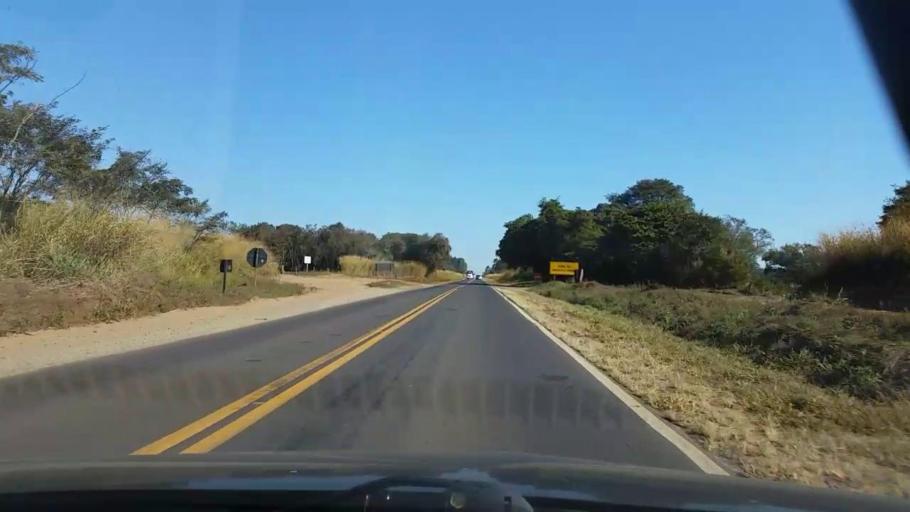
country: BR
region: Sao Paulo
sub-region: Avare
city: Avare
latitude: -22.9145
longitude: -48.7776
